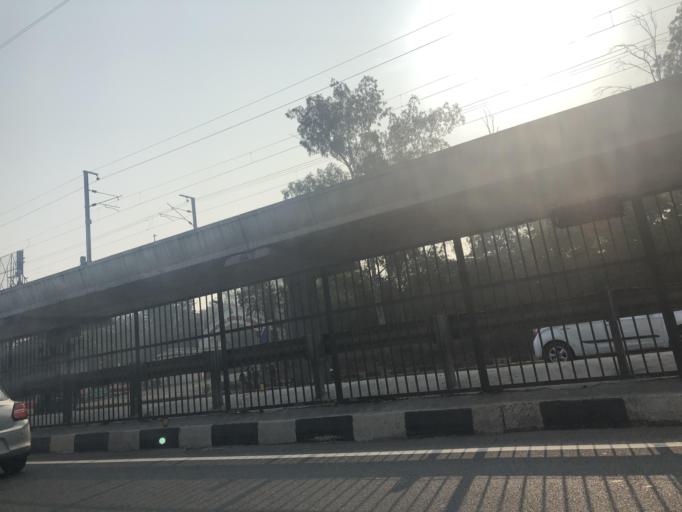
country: IN
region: NCT
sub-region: Central Delhi
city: Karol Bagh
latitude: 28.5899
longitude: 77.1554
